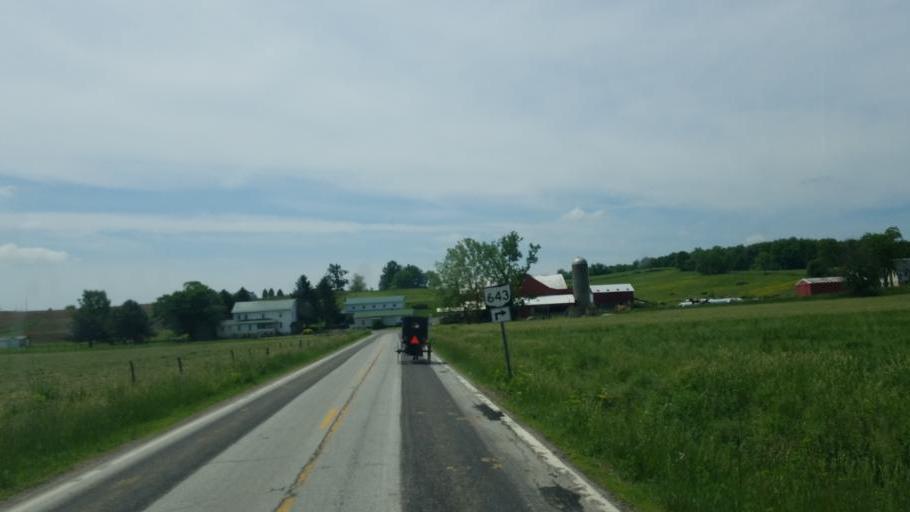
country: US
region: Ohio
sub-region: Tuscarawas County
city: Sugarcreek
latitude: 40.4661
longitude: -81.7018
